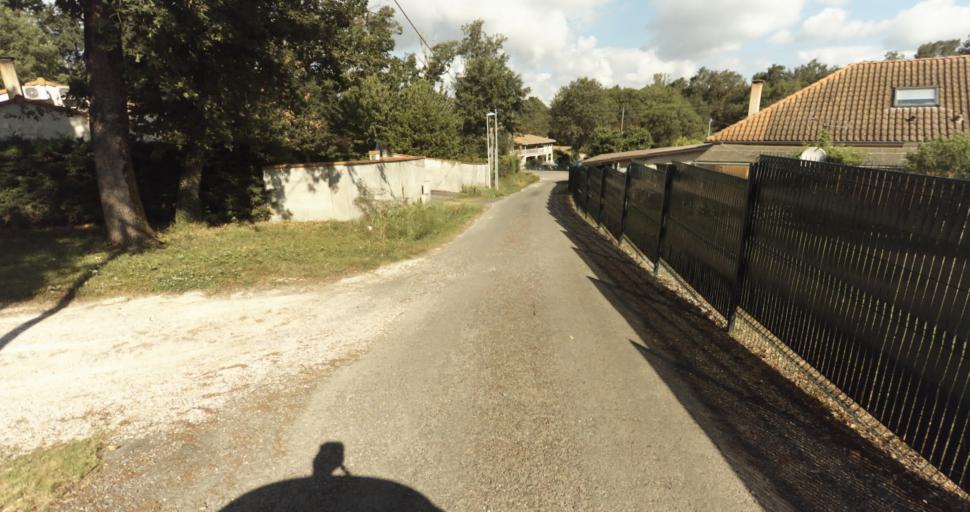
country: FR
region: Midi-Pyrenees
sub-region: Departement de la Haute-Garonne
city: Fonsorbes
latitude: 43.5621
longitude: 1.2189
